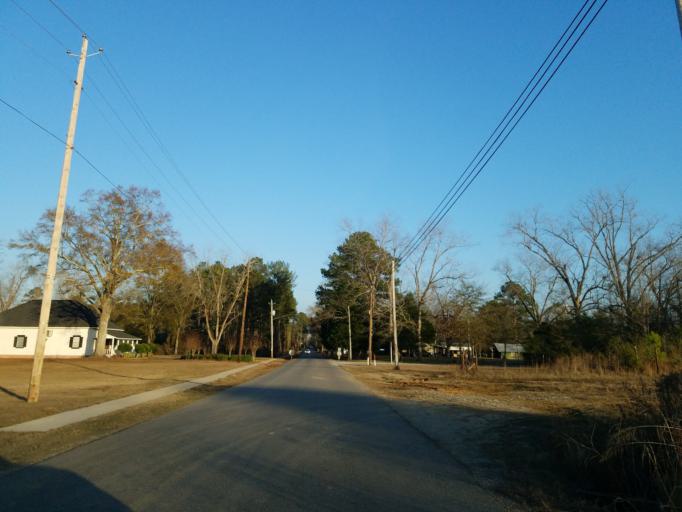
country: US
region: Mississippi
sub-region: Clarke County
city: Stonewall
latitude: 32.1742
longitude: -88.8292
